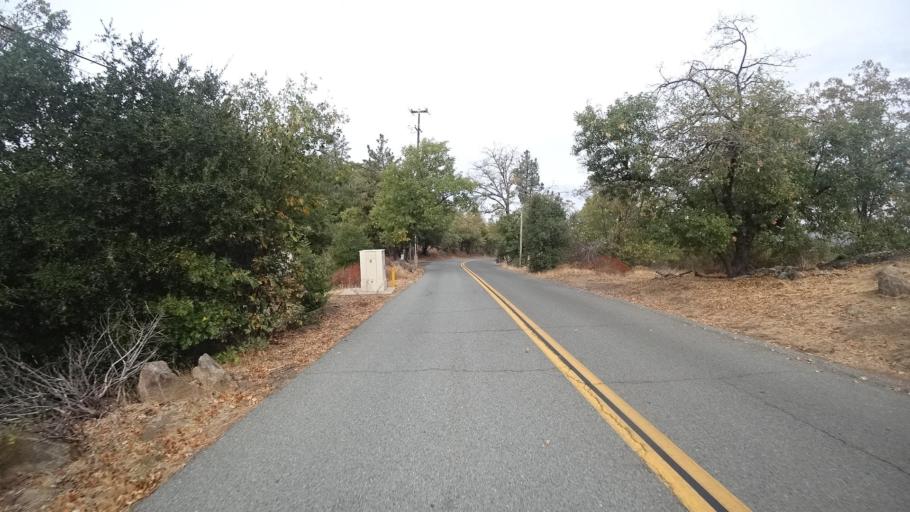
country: US
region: California
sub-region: San Diego County
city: Julian
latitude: 33.0561
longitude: -116.6033
